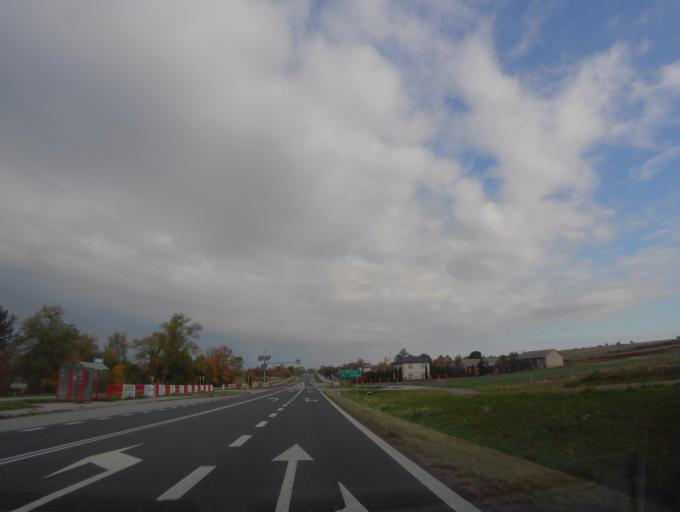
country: PL
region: Lublin Voivodeship
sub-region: Powiat lubelski
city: Wysokie
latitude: 50.8884
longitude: 22.6660
